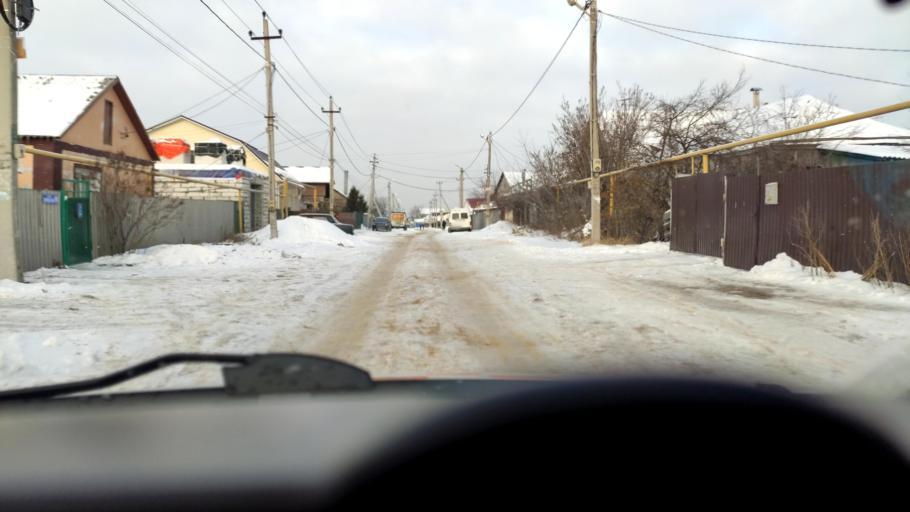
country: RU
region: Voronezj
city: Podgornoye
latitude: 51.7274
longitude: 39.1544
